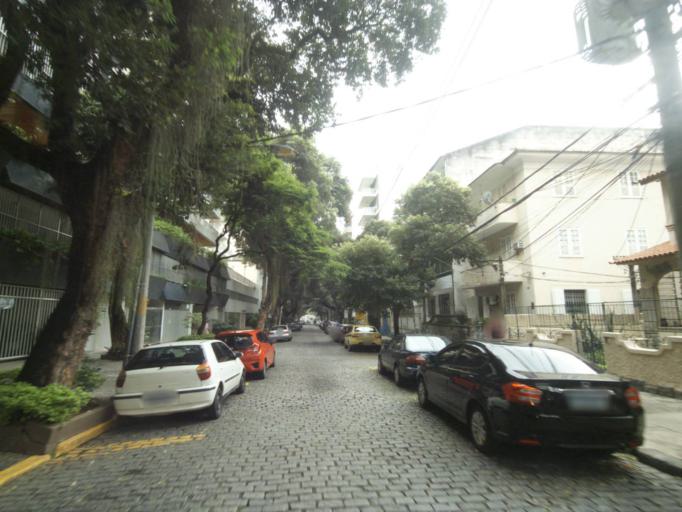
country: BR
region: Rio de Janeiro
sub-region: Rio De Janeiro
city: Rio de Janeiro
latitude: -22.9325
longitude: -43.2448
